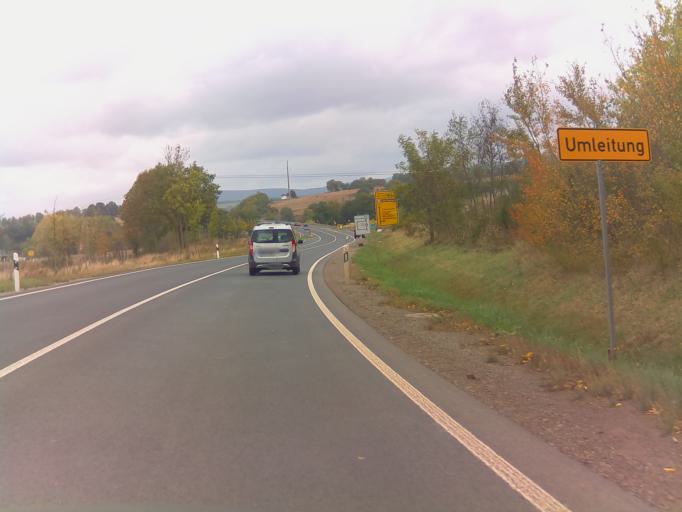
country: DE
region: Thuringia
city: Schwallungen
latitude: 50.7077
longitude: 10.3642
